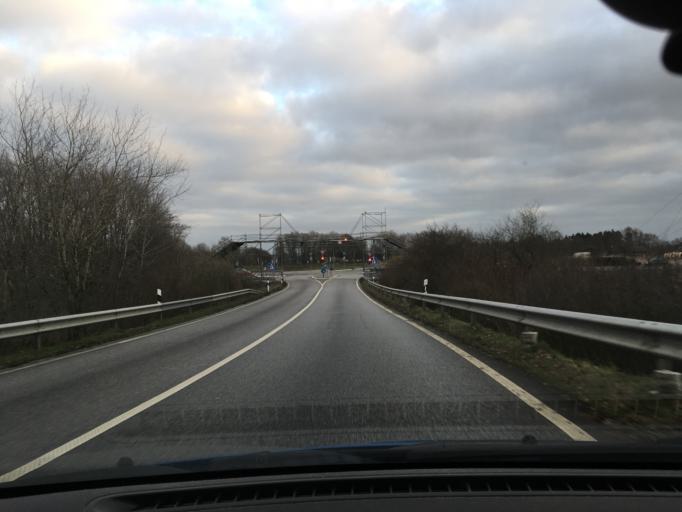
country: DE
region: Schleswig-Holstein
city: Hemmingstedt
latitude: 54.1679
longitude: 9.0882
